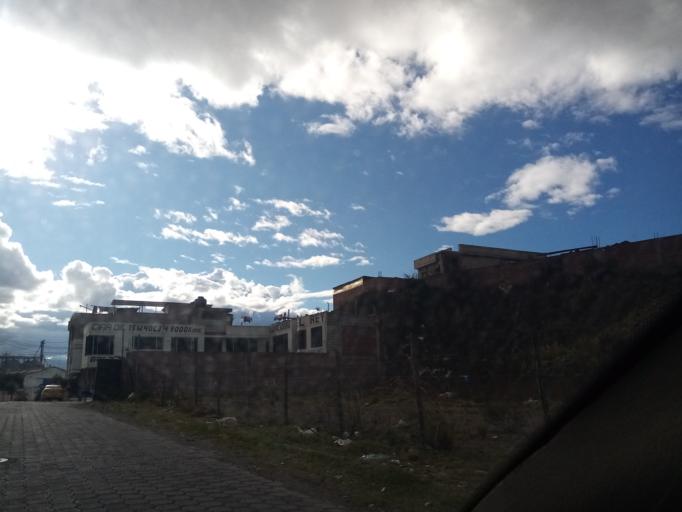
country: EC
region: Chimborazo
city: Riobamba
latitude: -1.6854
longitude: -78.6292
